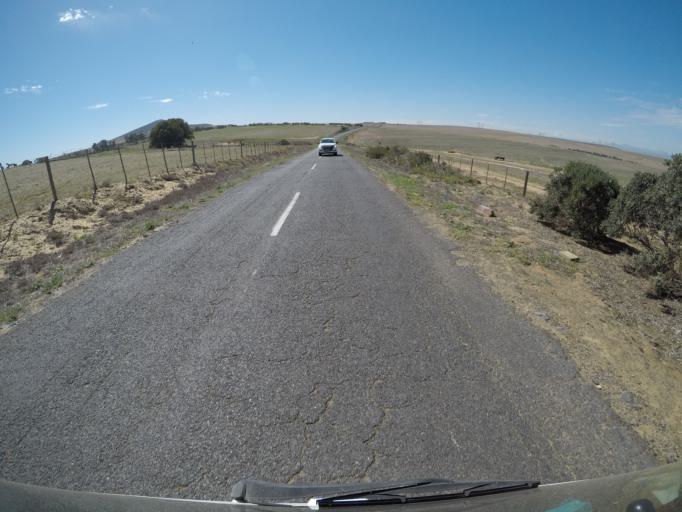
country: ZA
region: Western Cape
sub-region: City of Cape Town
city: Sunset Beach
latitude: -33.7444
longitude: 18.5603
